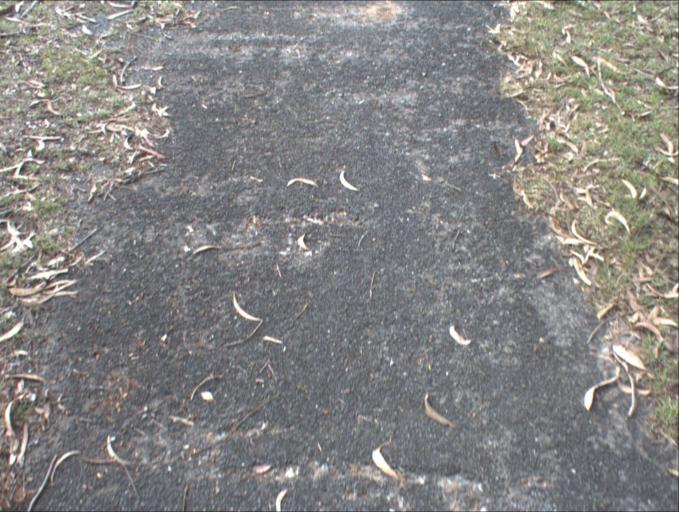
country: AU
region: Queensland
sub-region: Logan
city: Cedar Vale
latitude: -27.8335
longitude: 153.0282
